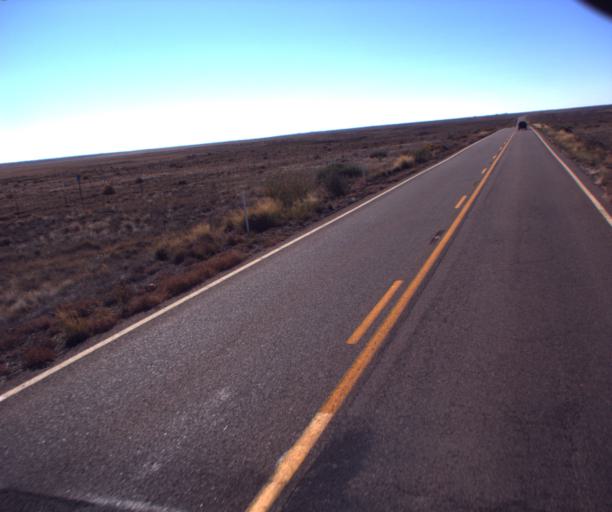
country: US
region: Arizona
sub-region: Navajo County
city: Dilkon
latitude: 35.2609
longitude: -110.4297
